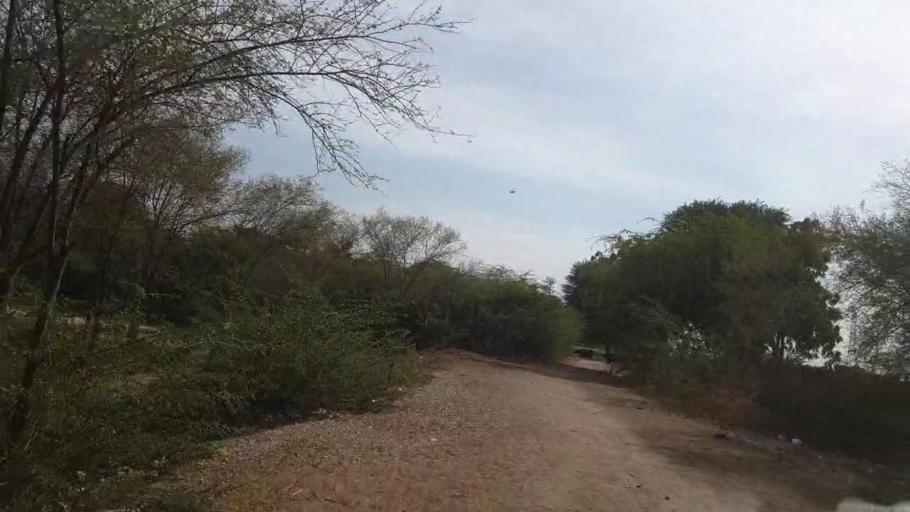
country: PK
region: Sindh
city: Nabisar
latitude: 25.0463
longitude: 69.5710
